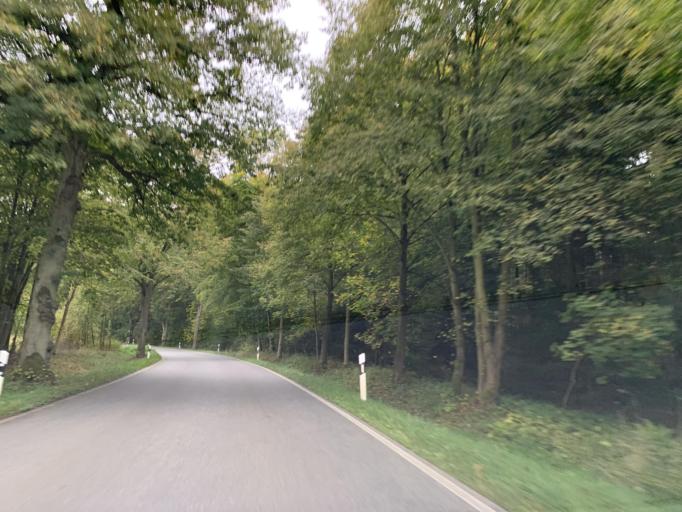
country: DE
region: Mecklenburg-Vorpommern
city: Burg Stargard
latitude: 53.4910
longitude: 13.2974
